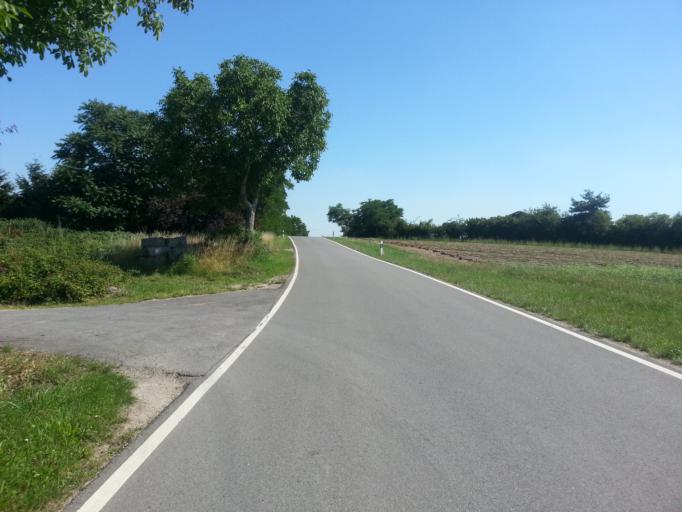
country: DE
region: Hesse
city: Viernheim
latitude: 49.5236
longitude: 8.5798
